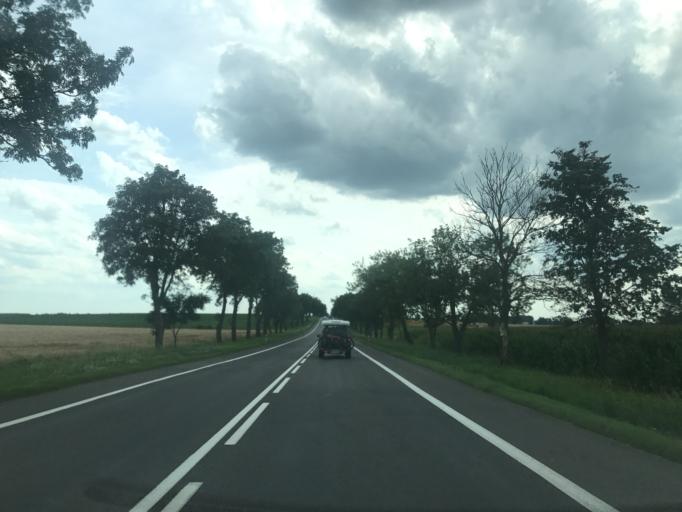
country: PL
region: Masovian Voivodeship
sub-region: Powiat mlawski
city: Wisniewo
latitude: 53.0484
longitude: 20.3432
